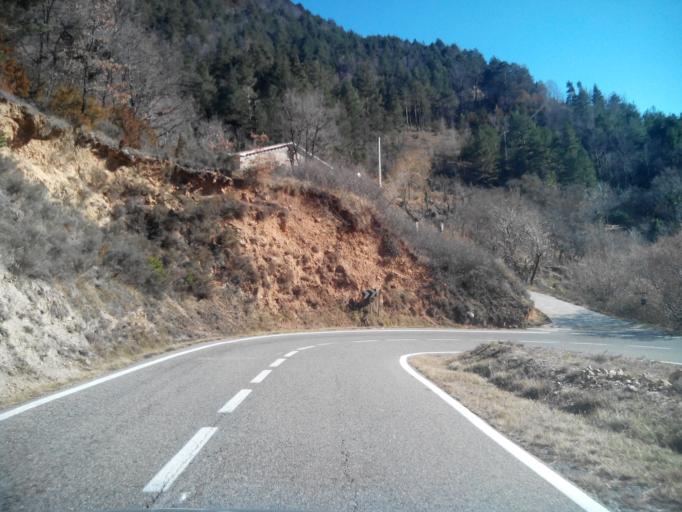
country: ES
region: Catalonia
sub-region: Provincia de Barcelona
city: Capolat
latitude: 42.0978
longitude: 1.7511
